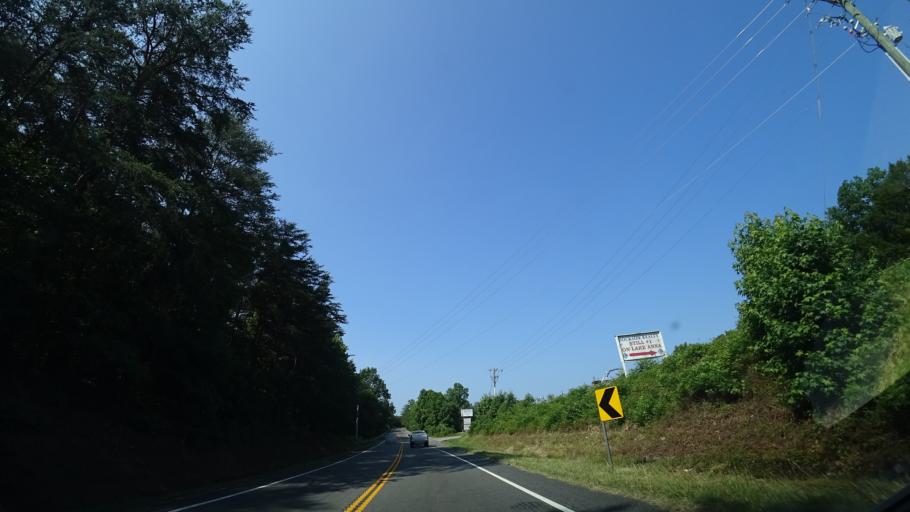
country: US
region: Virginia
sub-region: Louisa County
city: Louisa
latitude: 38.0894
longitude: -77.8080
